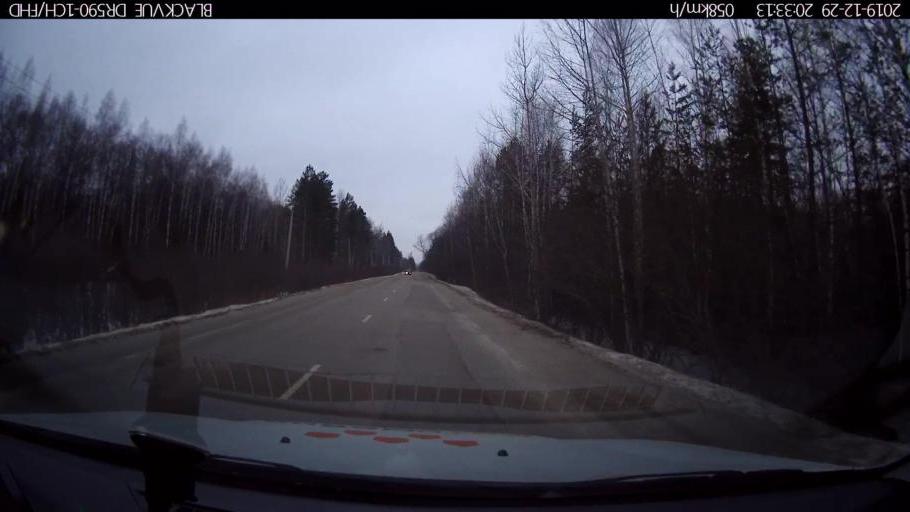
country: RU
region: Nizjnij Novgorod
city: Afonino
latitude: 56.1793
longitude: 44.0546
